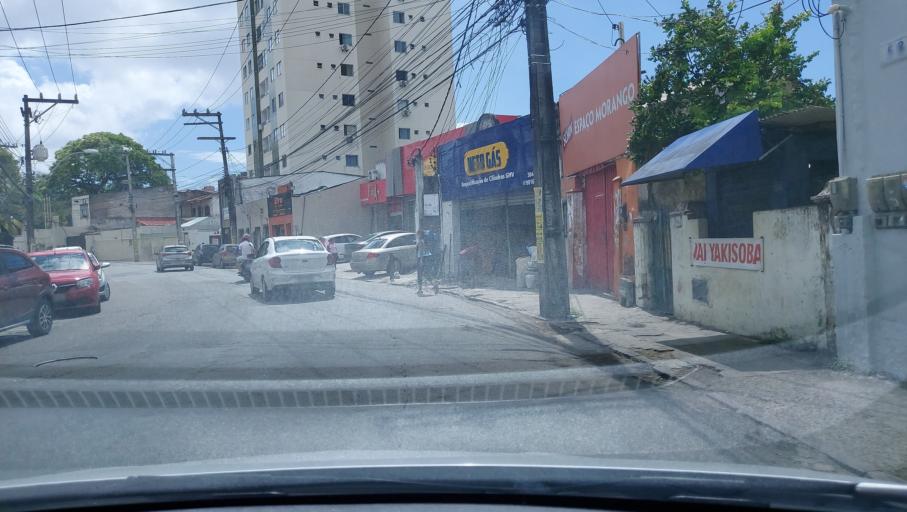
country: BR
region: Bahia
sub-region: Salvador
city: Salvador
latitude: -12.9789
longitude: -38.4986
